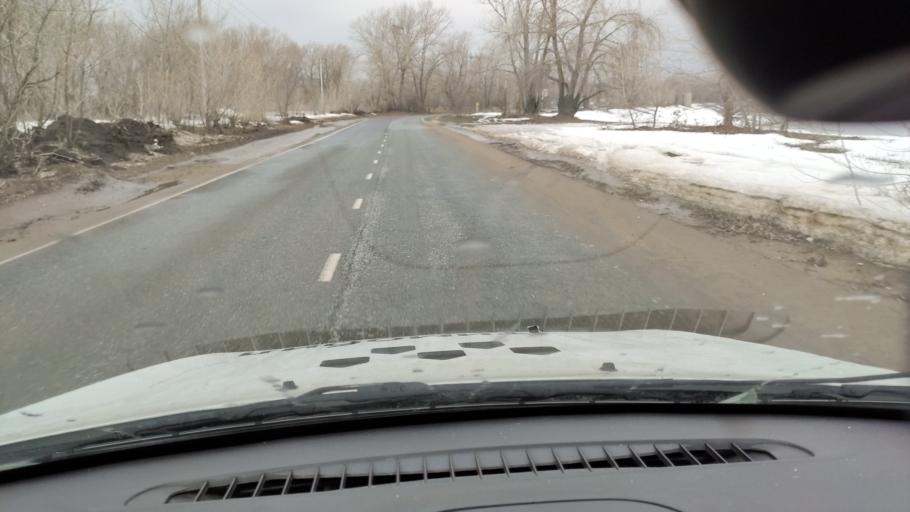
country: RU
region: Samara
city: Zhigulevsk
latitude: 53.4609
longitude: 49.5117
